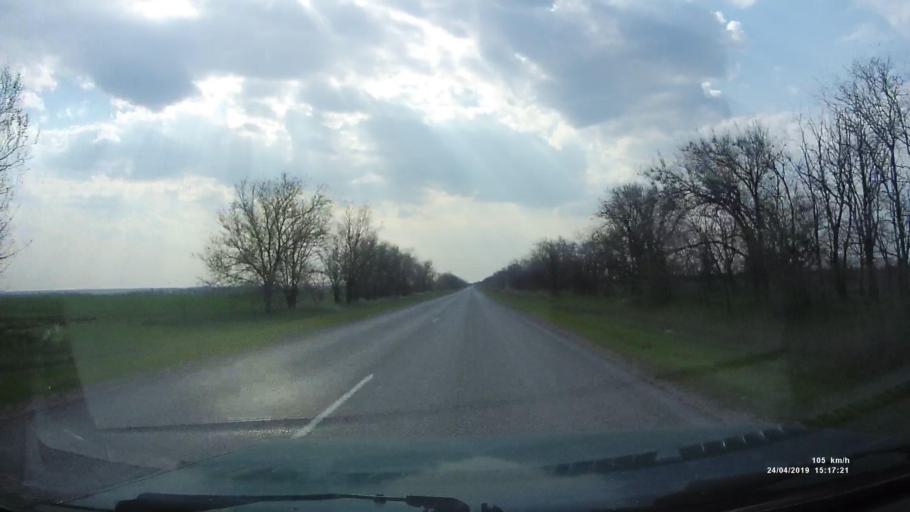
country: RU
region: Rostov
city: Remontnoye
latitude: 46.5465
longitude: 43.1918
